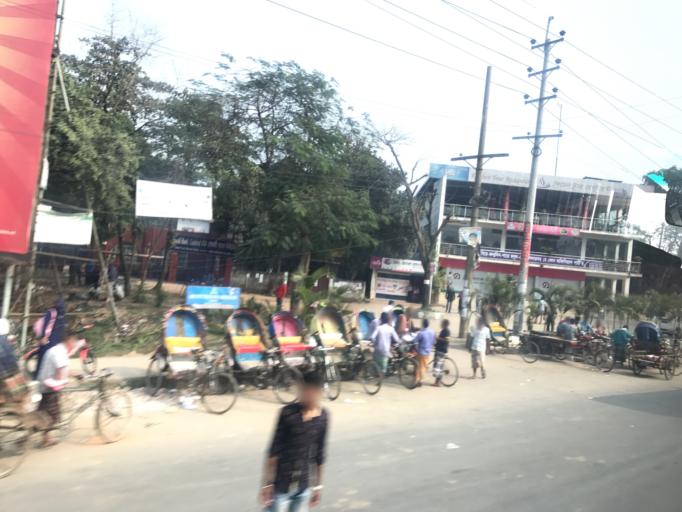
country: BD
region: Dhaka
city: Tungi
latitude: 23.9119
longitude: 90.2607
